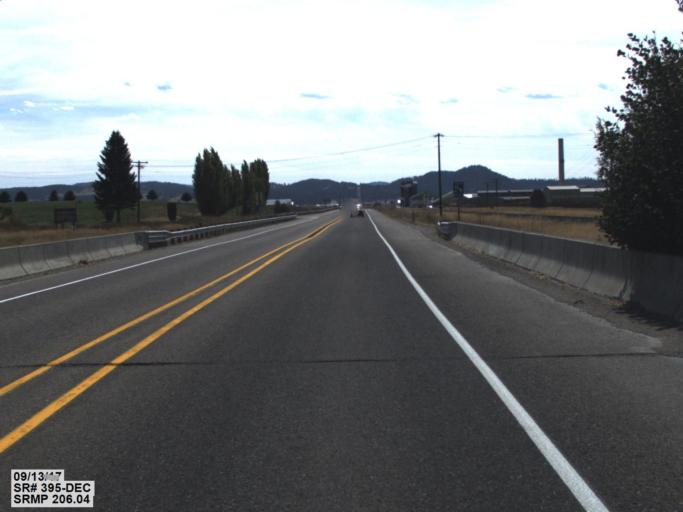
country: US
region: Washington
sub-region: Stevens County
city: Chewelah
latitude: 48.2606
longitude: -117.7154
